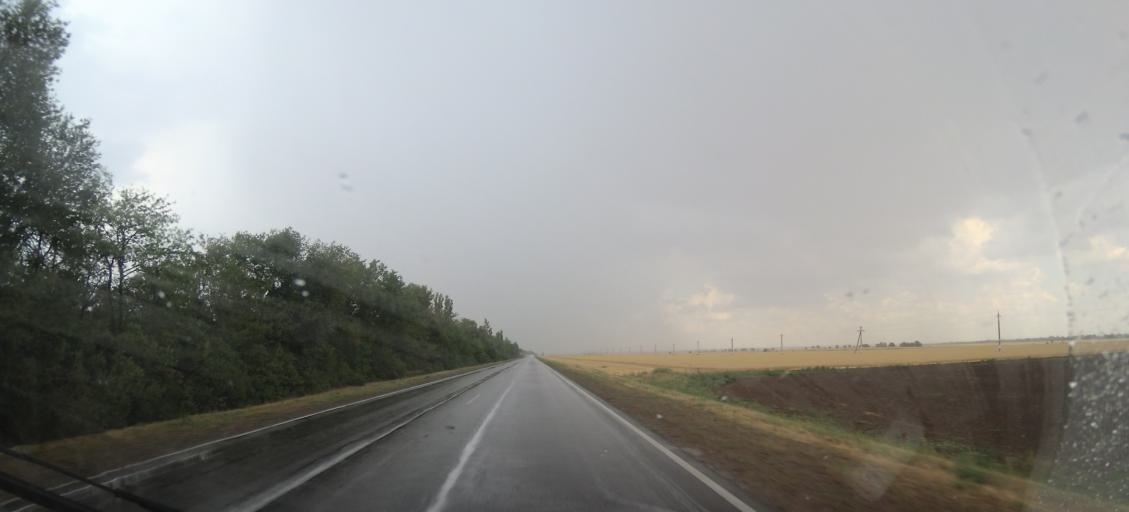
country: RU
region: Rostov
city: Proletarsk
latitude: 46.6617
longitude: 41.6861
